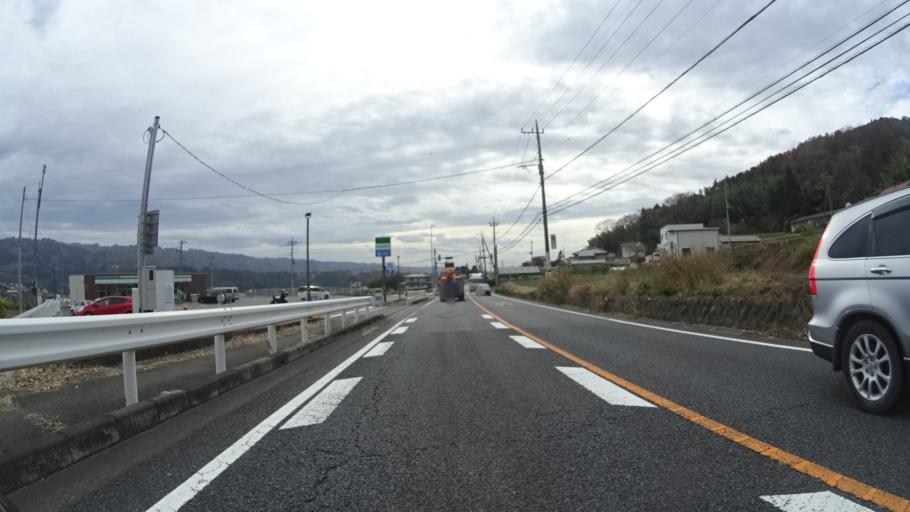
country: JP
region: Gunma
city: Numata
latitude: 36.5613
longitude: 139.0378
